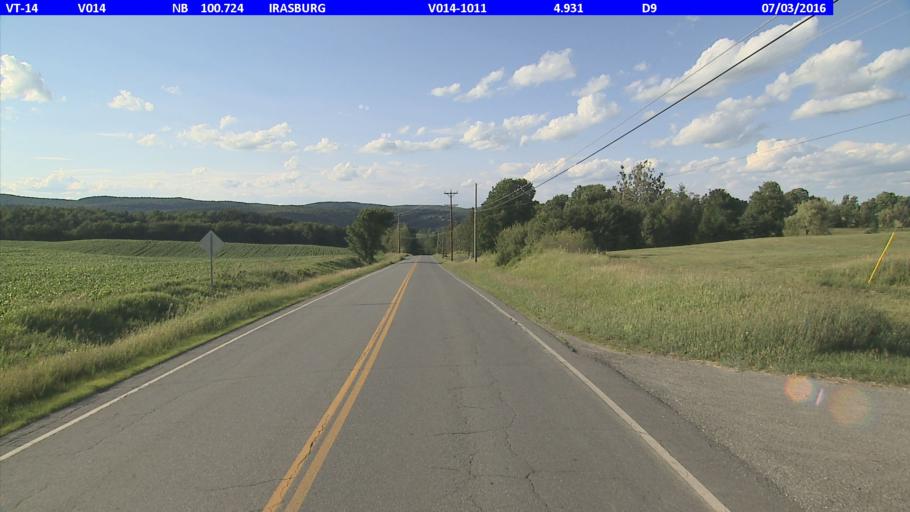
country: US
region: Vermont
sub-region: Orleans County
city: Newport
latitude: 44.8300
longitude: -72.2909
